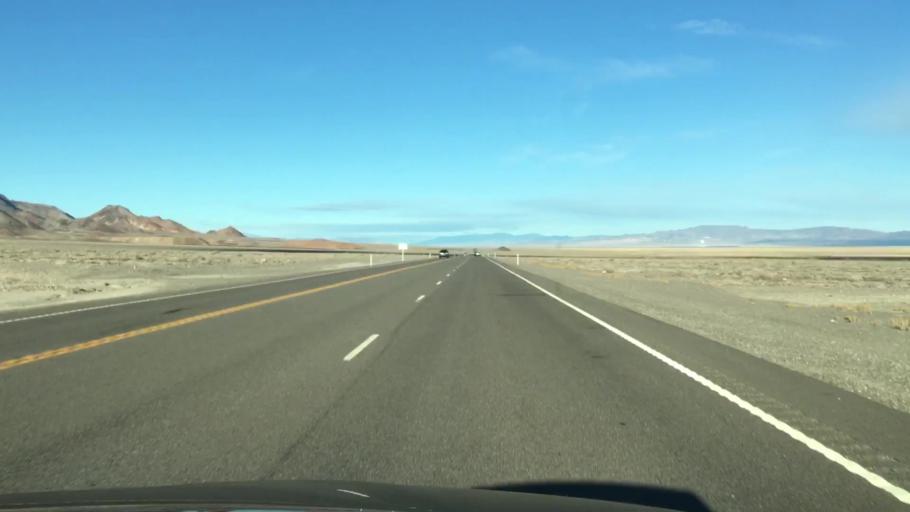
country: US
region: Nevada
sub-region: Nye County
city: Tonopah
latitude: 38.0523
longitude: -117.6543
